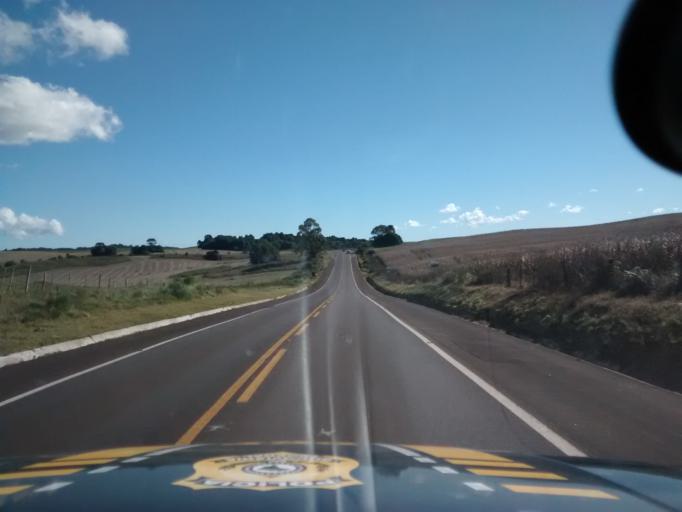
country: BR
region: Rio Grande do Sul
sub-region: Lagoa Vermelha
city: Lagoa Vermelha
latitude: -28.3264
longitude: -51.2666
